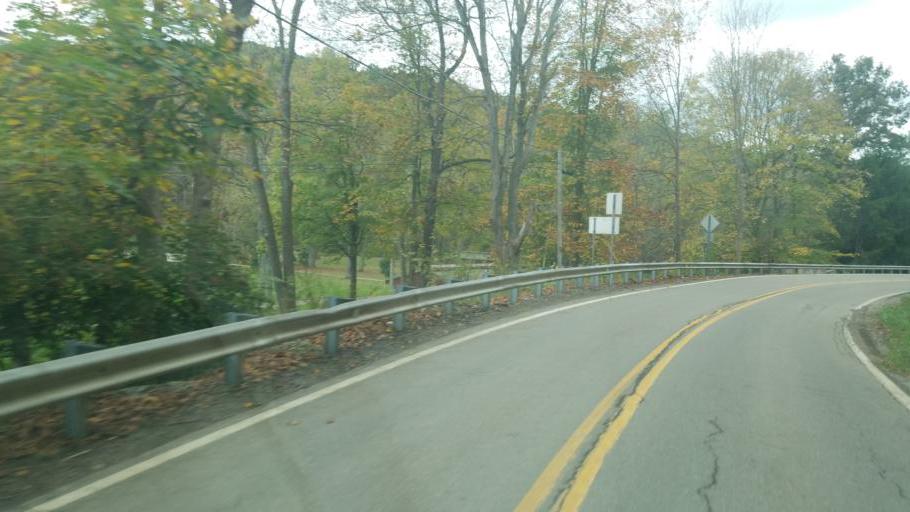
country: US
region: Ohio
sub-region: Knox County
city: Danville
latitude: 40.5193
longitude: -82.1007
